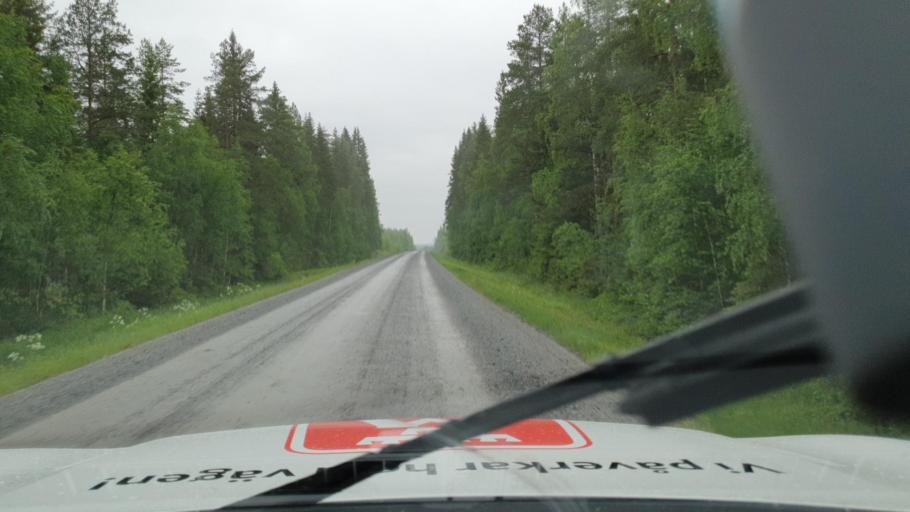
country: SE
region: Vaesterbotten
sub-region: Nordmalings Kommun
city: Nordmaling
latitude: 63.8293
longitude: 19.4886
